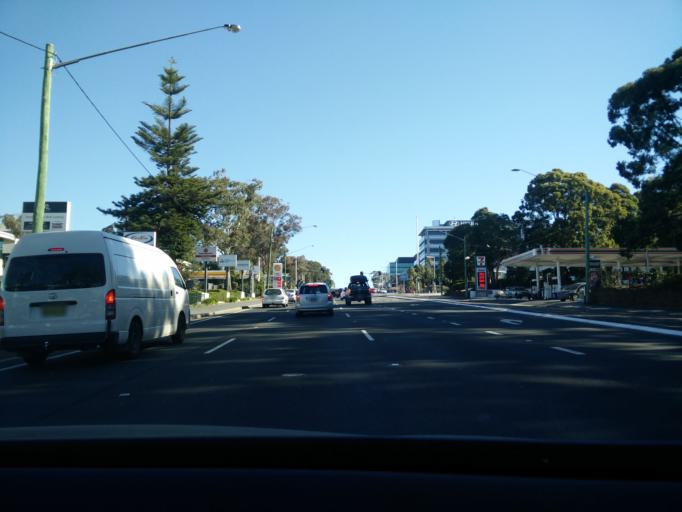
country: AU
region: New South Wales
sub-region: Ryde
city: North Ryde
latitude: -33.7840
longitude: 151.1296
